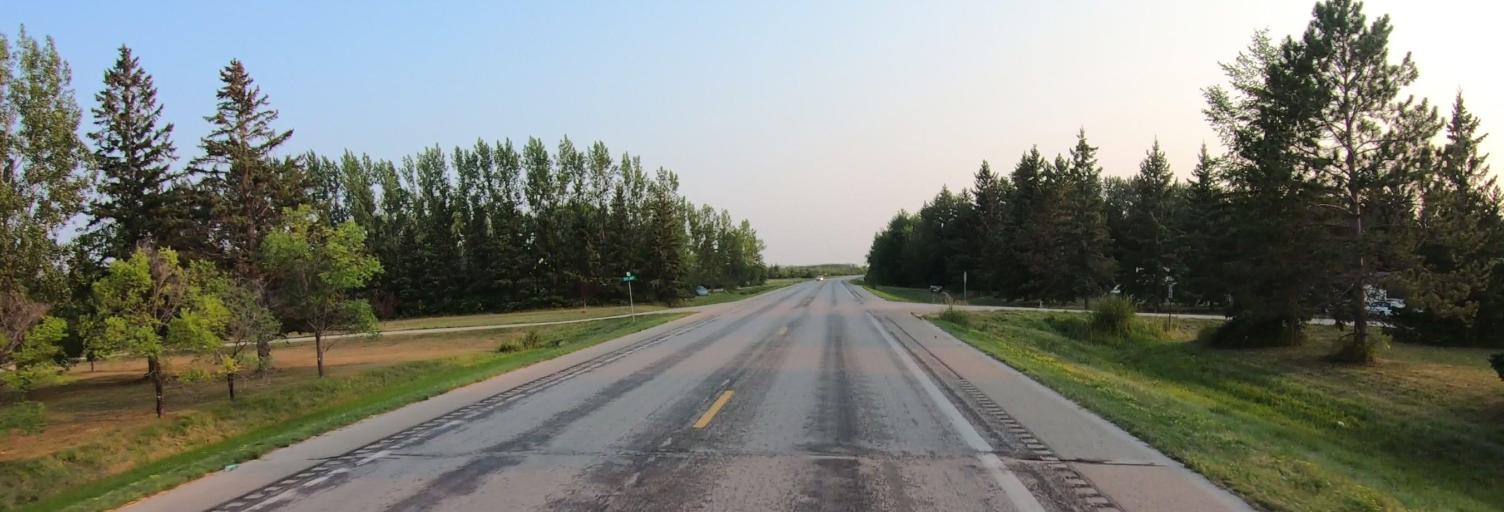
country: US
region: Minnesota
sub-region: Roseau County
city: Warroad
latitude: 48.8766
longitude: -95.3209
